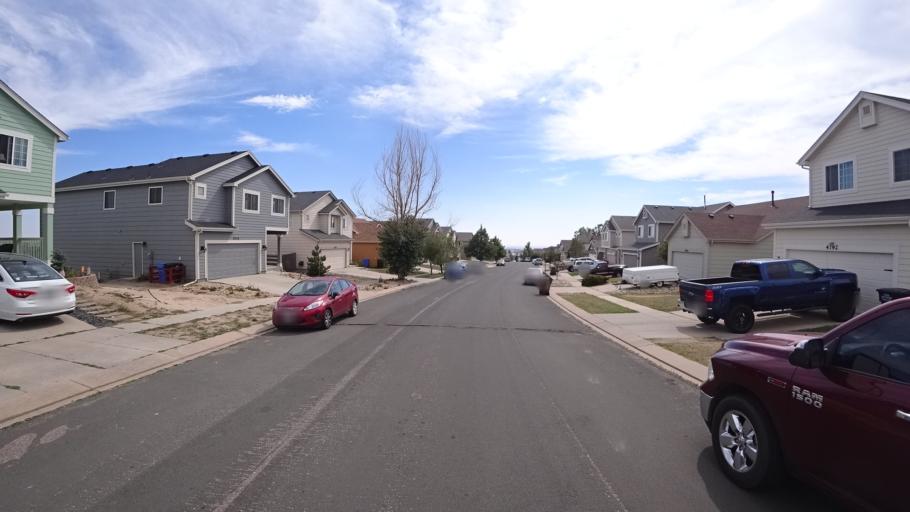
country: US
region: Colorado
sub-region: El Paso County
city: Cimarron Hills
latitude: 38.9007
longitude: -104.7176
